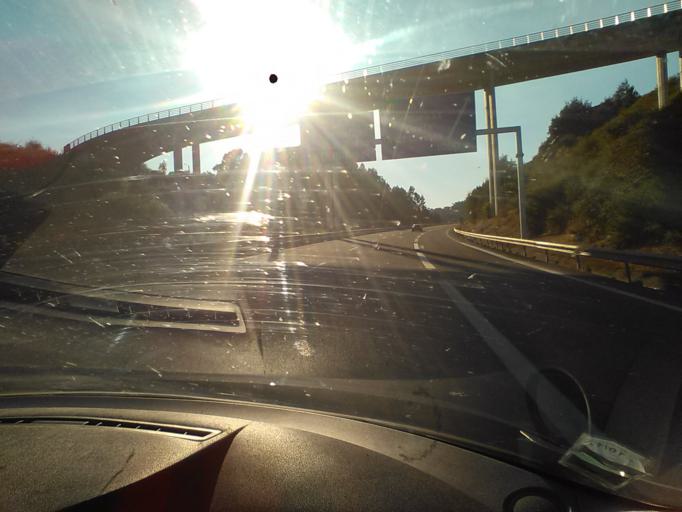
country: PT
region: Braga
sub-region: Guimaraes
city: Serzedo
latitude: 41.3977
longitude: -8.2414
